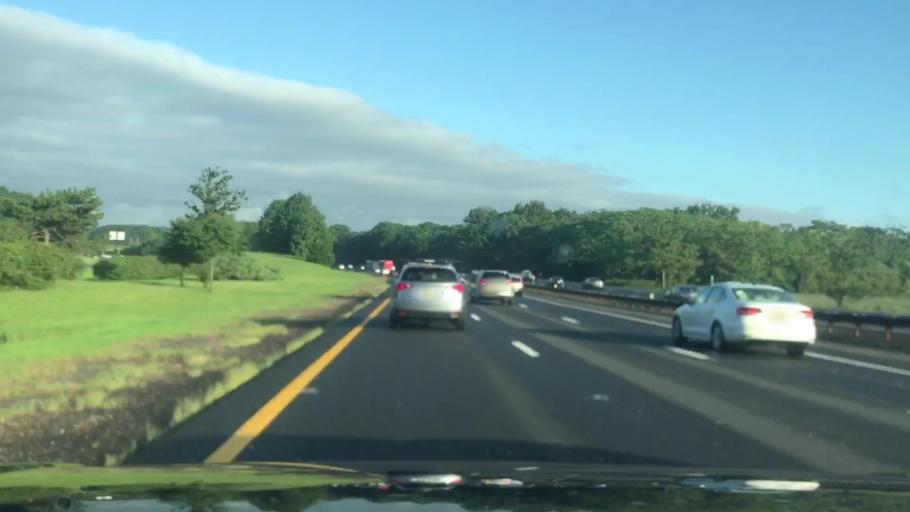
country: US
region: New Jersey
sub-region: Monmouth County
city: Matawan
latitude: 40.4263
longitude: -74.2224
